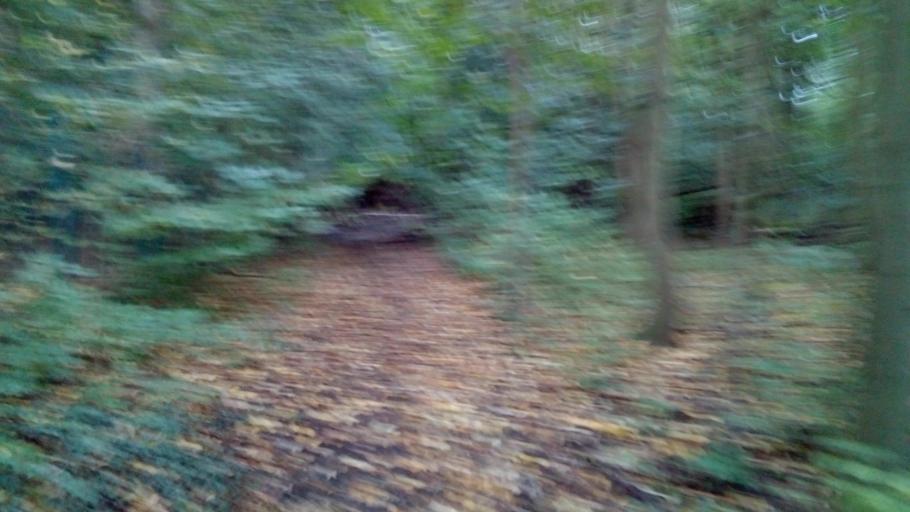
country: DE
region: North Rhine-Westphalia
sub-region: Regierungsbezirk Arnsberg
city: Bochum
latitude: 51.4428
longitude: 7.2788
